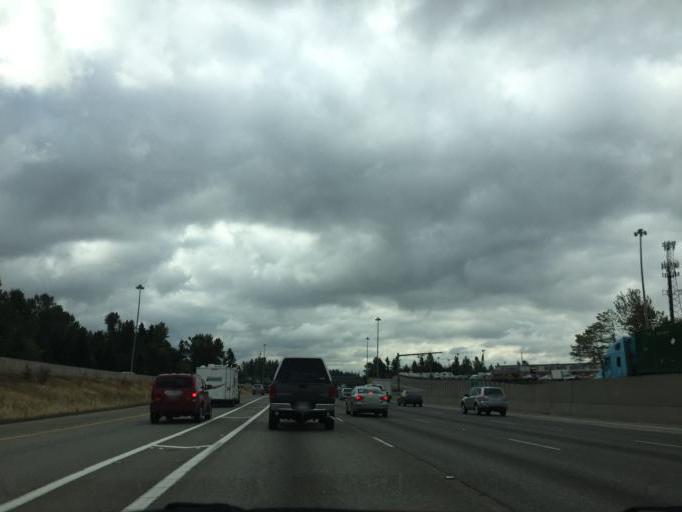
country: US
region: Washington
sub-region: King County
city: Lakeland South
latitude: 47.2835
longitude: -122.3089
